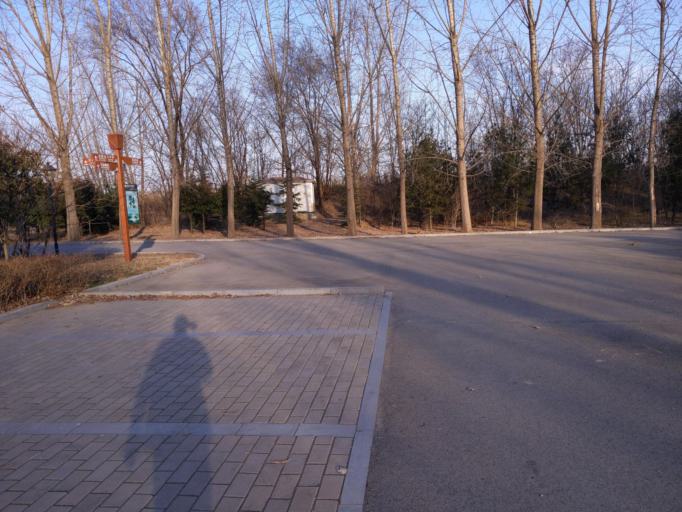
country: CN
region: Henan Sheng
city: Puyang
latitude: 35.7797
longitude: 114.9538
